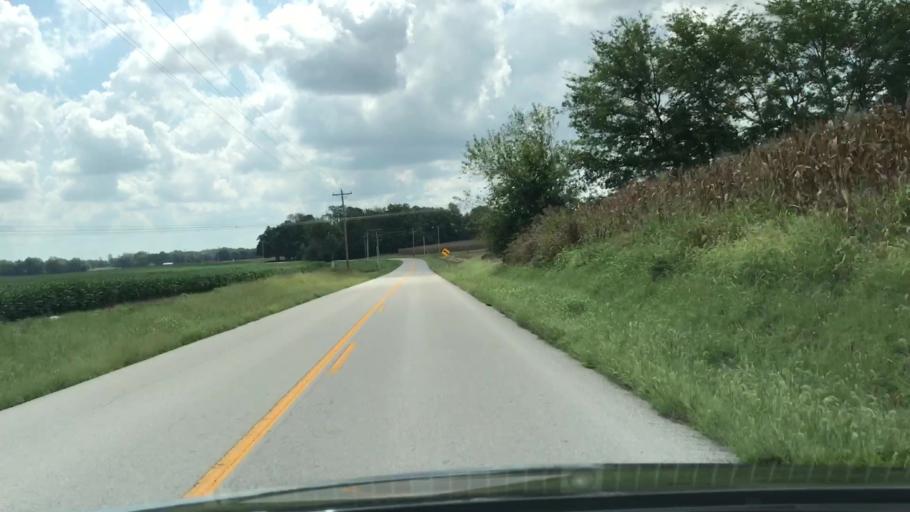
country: US
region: Kentucky
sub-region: Todd County
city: Elkton
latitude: 36.7743
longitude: -87.1183
